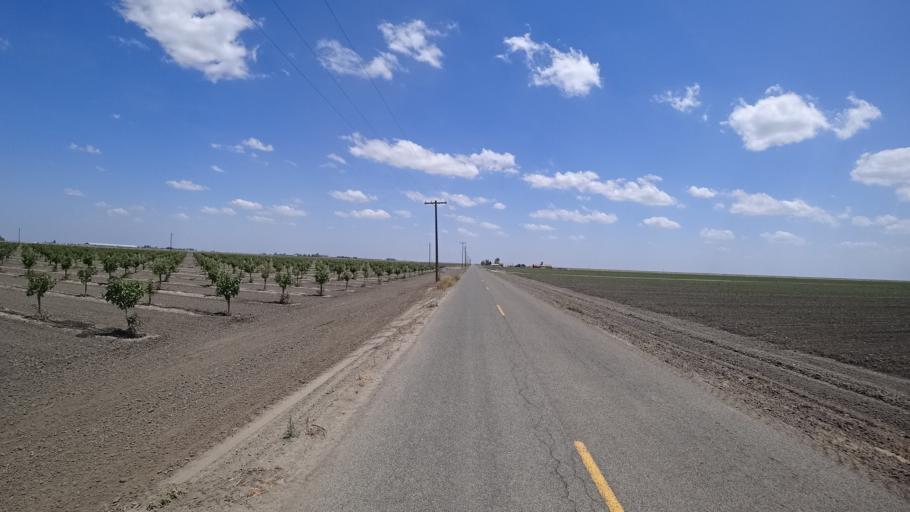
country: US
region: California
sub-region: Kings County
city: Stratford
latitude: 36.1527
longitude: -119.8087
